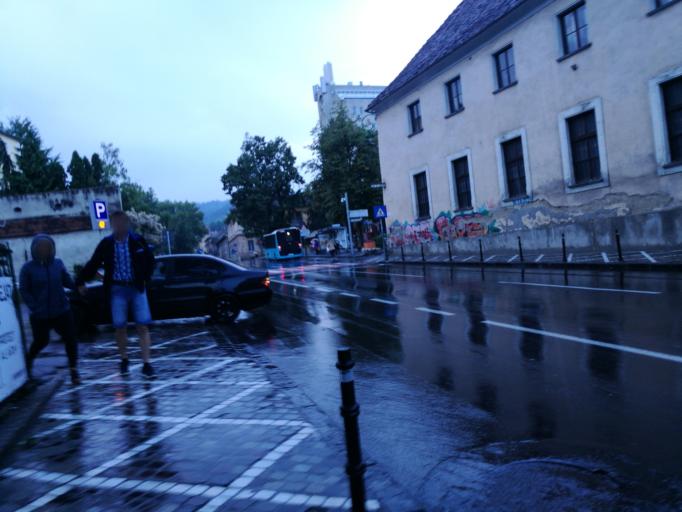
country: RO
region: Brasov
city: Brasov
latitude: 45.6405
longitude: 25.5863
